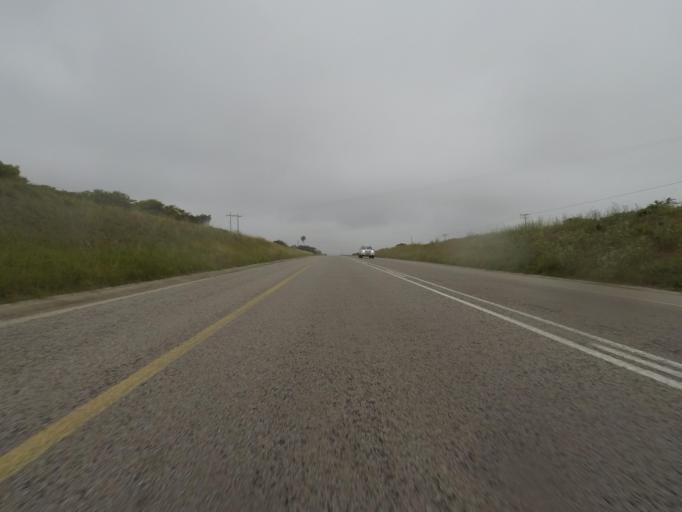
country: ZA
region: Eastern Cape
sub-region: Cacadu District Municipality
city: Grahamstown
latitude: -33.6504
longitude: 26.3912
